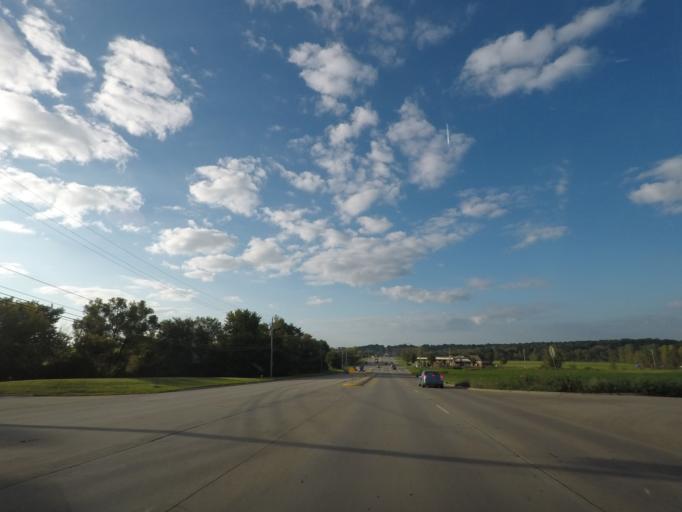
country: US
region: Iowa
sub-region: Warren County
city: Norwalk
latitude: 41.5140
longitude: -93.6450
